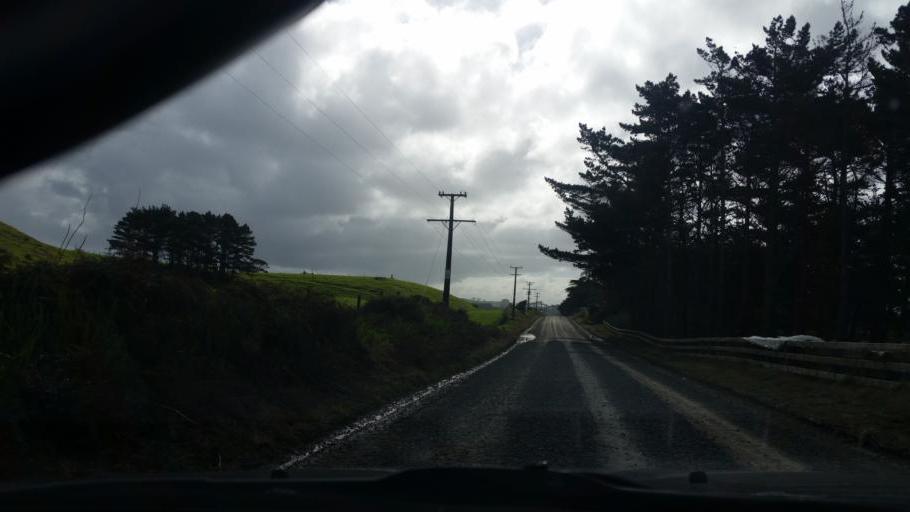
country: NZ
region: Northland
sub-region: Kaipara District
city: Dargaville
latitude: -36.0612
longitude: 173.8762
